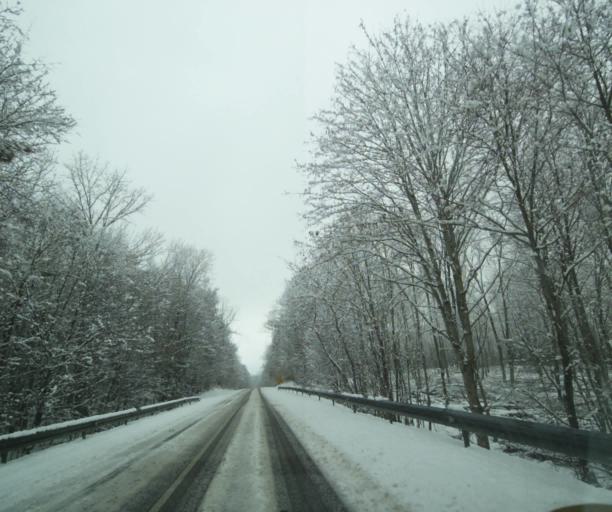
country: FR
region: Champagne-Ardenne
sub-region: Departement de la Haute-Marne
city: Montier-en-Der
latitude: 48.5294
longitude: 4.7902
